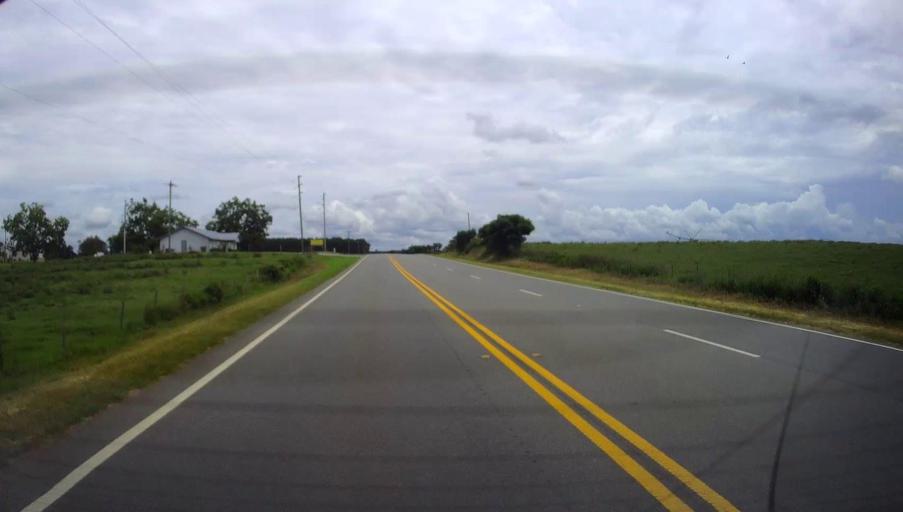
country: US
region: Georgia
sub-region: Macon County
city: Montezuma
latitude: 32.2924
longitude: -83.9360
